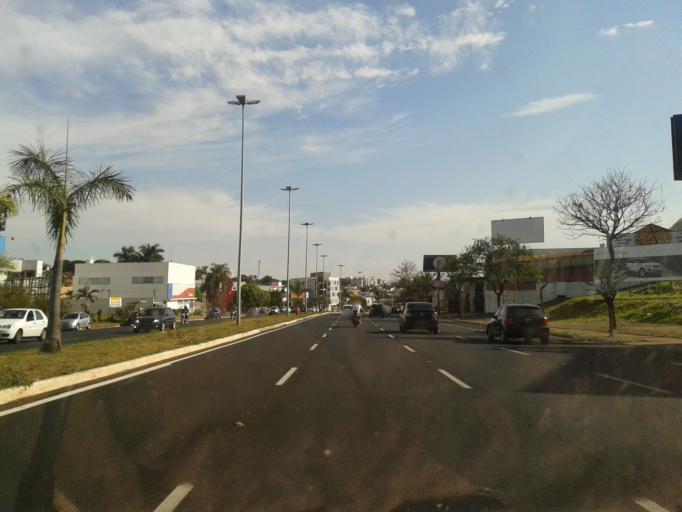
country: BR
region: Minas Gerais
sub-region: Uberlandia
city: Uberlandia
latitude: -18.9267
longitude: -48.2742
